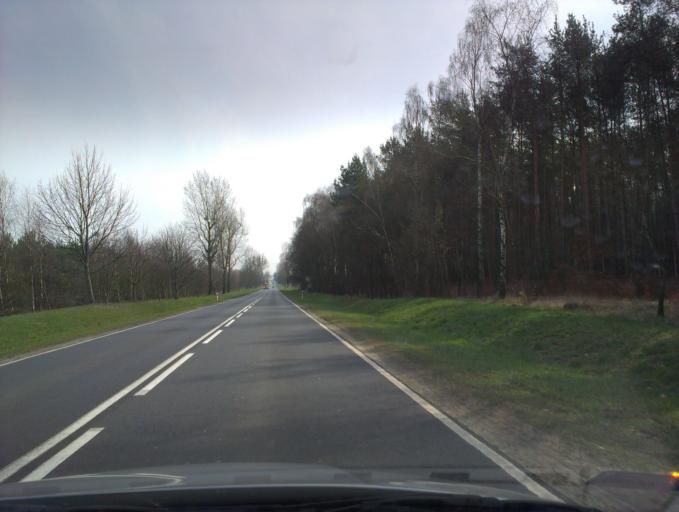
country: PL
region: Greater Poland Voivodeship
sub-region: Powiat pilski
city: Smilowo
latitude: 53.1383
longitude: 16.8993
